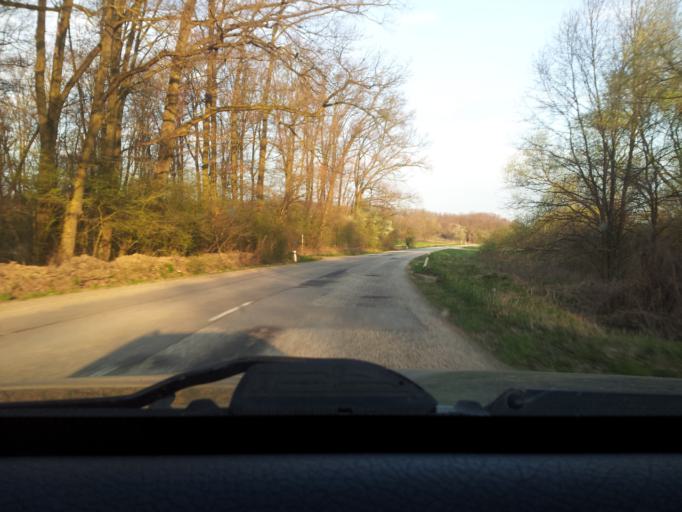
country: SK
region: Nitriansky
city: Tlmace
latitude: 48.2794
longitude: 18.4836
